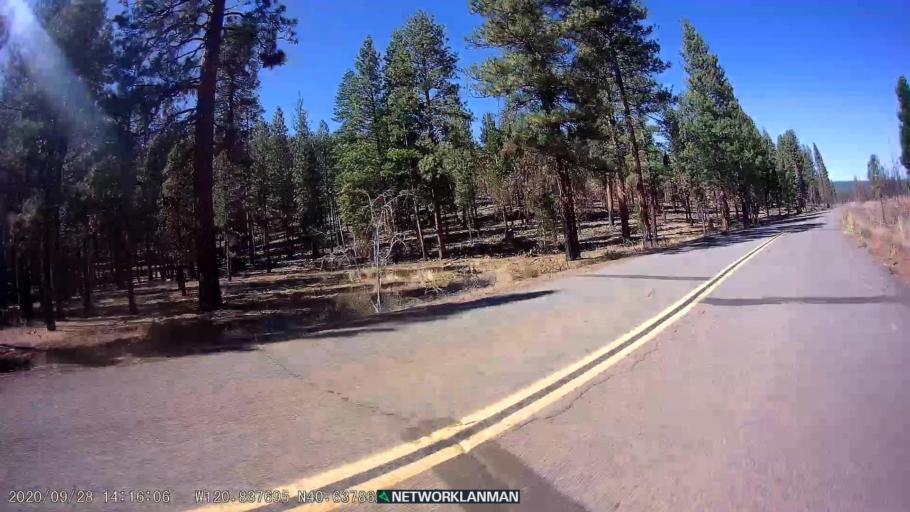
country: US
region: California
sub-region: Lassen County
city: Susanville
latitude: 40.6381
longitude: -120.8377
